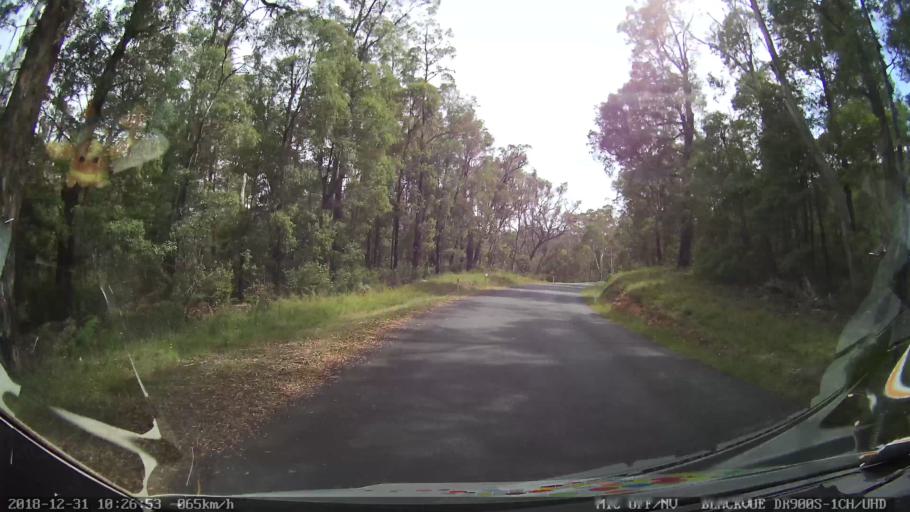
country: AU
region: New South Wales
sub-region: Snowy River
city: Jindabyne
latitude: -36.4908
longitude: 148.1400
